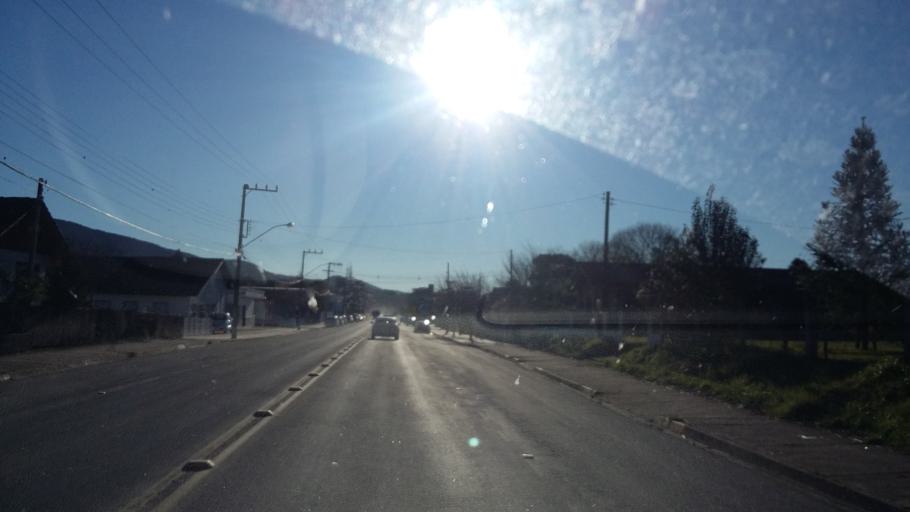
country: BR
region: Santa Catarina
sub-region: Lauro Muller
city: Lauro Muller
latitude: -27.9919
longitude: -49.5775
